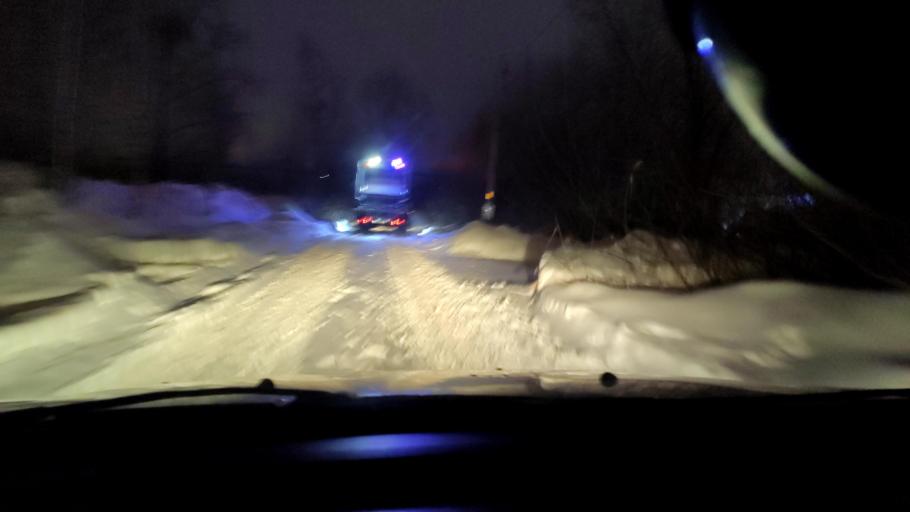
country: RU
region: Perm
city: Kondratovo
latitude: 58.0367
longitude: 56.0432
